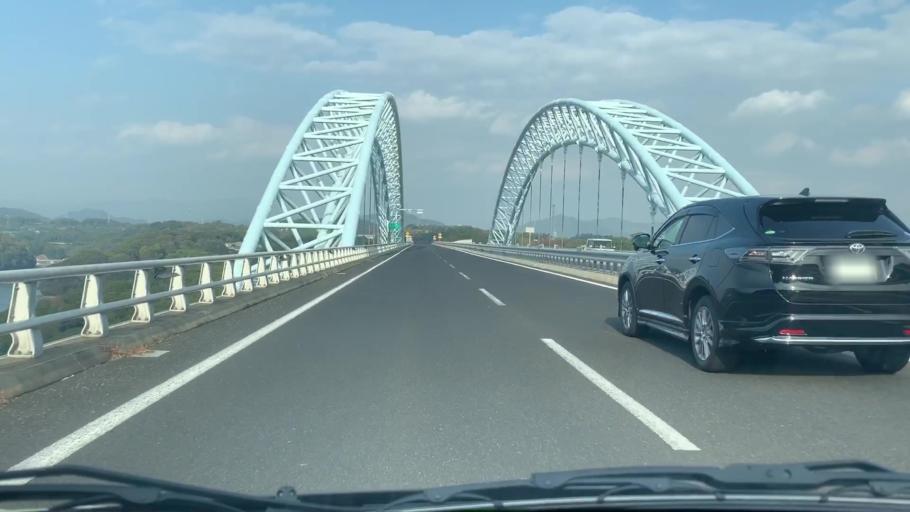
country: JP
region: Nagasaki
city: Sasebo
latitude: 33.0532
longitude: 129.7544
